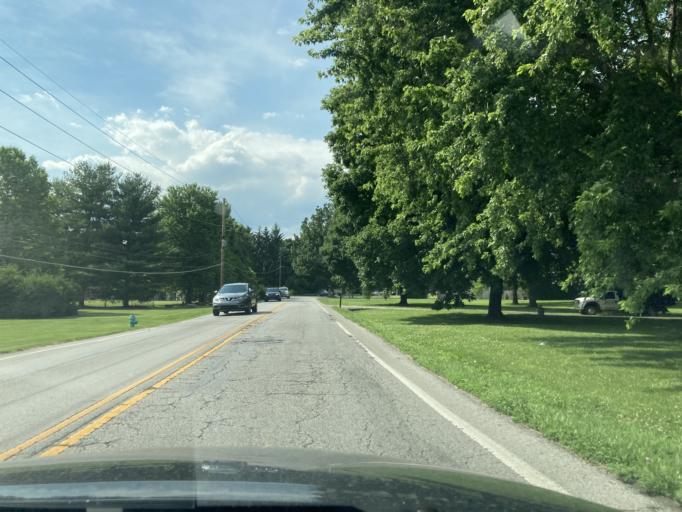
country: US
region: Indiana
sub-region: Marion County
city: Speedway
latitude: 39.8379
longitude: -86.2298
